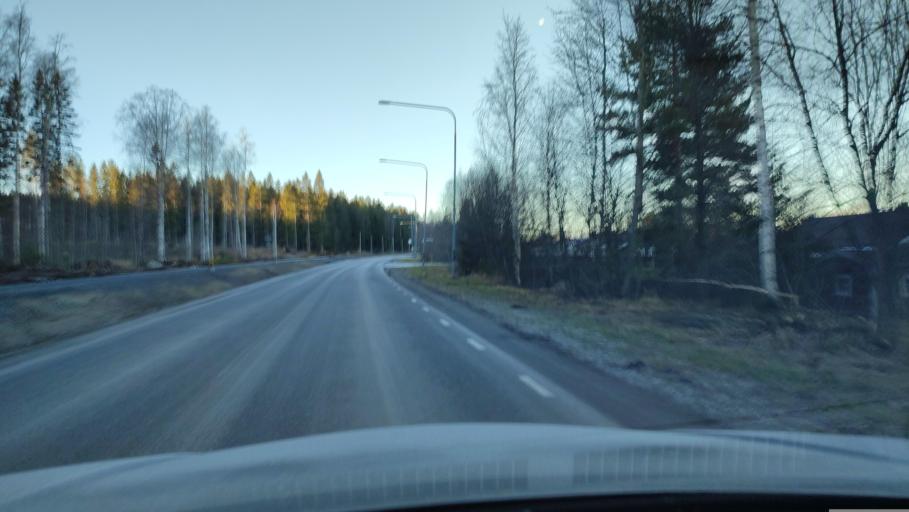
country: SE
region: Vaesterbotten
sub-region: Skelleftea Kommun
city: Viken
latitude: 64.7399
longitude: 20.9290
